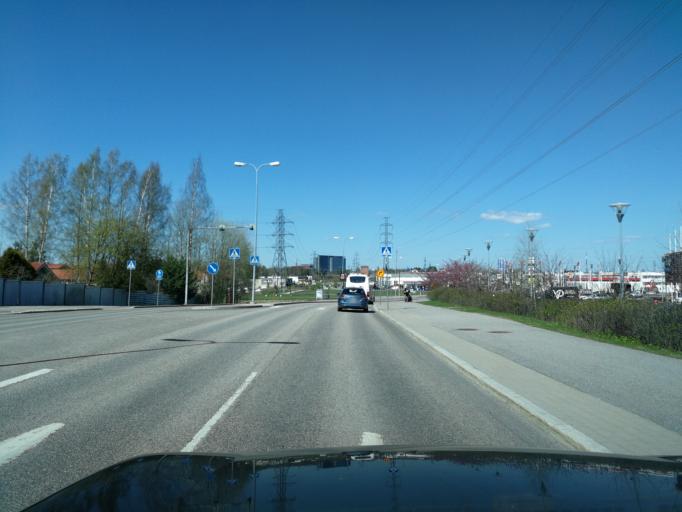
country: FI
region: Uusimaa
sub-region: Helsinki
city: Vantaa
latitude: 60.2779
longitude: 24.9706
